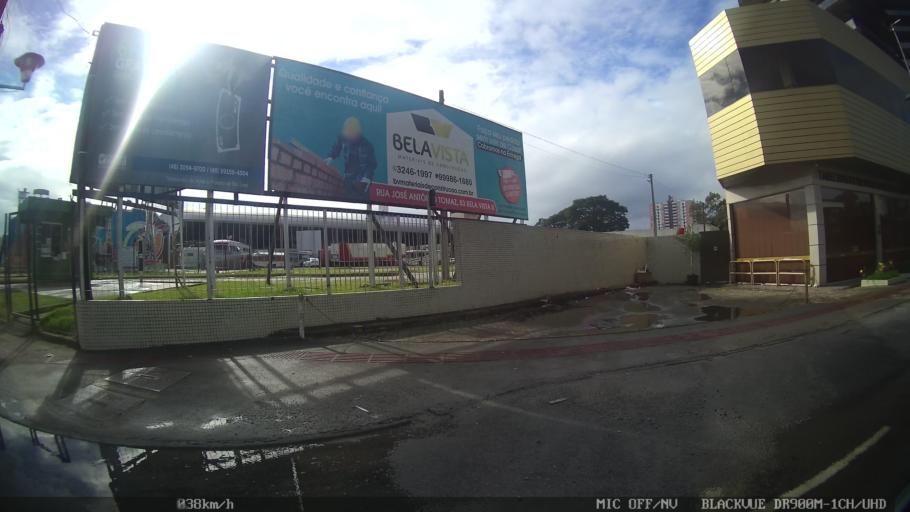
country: BR
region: Santa Catarina
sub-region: Sao Jose
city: Campinas
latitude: -27.5859
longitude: -48.6130
